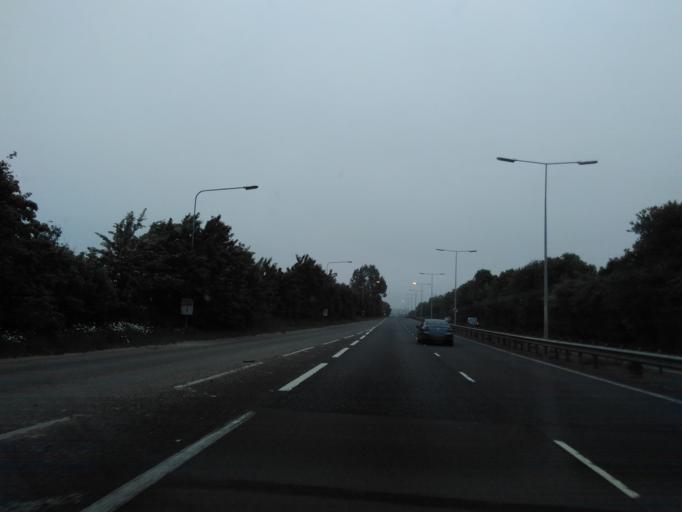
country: GB
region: England
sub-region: Kent
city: Dunkirk
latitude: 51.3174
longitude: 0.9630
